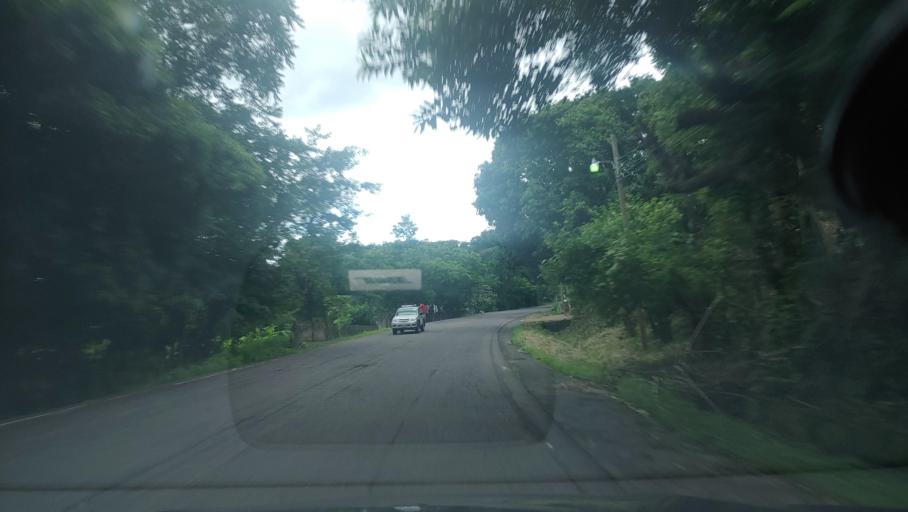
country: HN
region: Choluteca
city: Corpus
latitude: 13.3690
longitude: -87.0273
